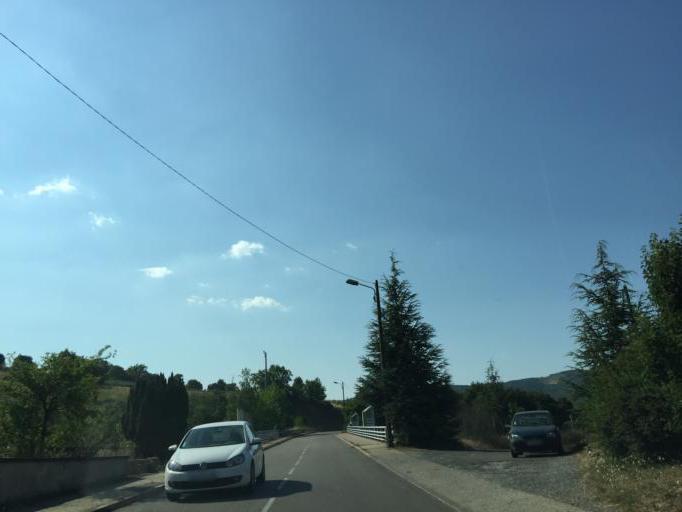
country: FR
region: Rhone-Alpes
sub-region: Departement de la Loire
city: Saint-Chamond
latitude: 45.4837
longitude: 4.5024
